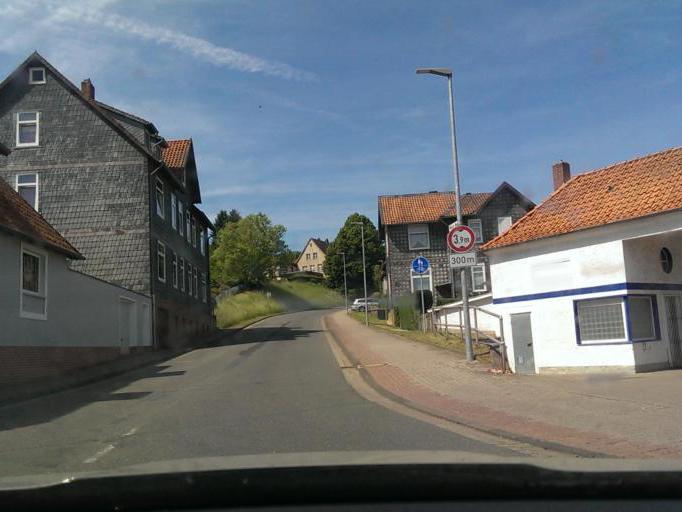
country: DE
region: Lower Saxony
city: Alfeld
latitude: 51.9841
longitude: 9.8085
